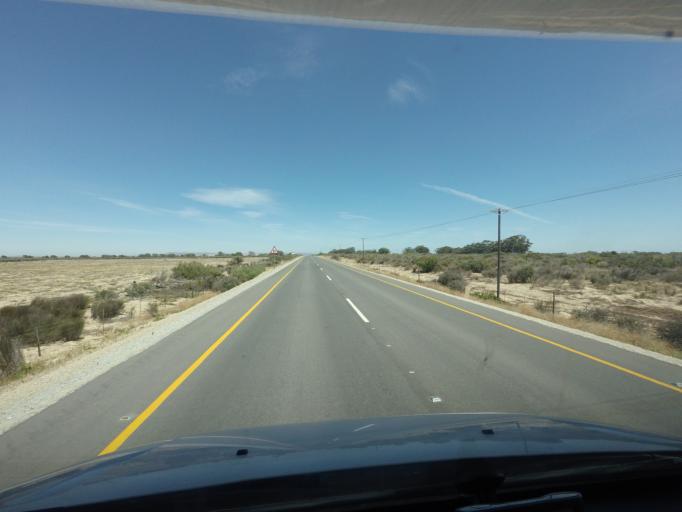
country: ZA
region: Western Cape
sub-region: West Coast District Municipality
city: Vredenburg
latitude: -32.7953
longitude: 18.2494
